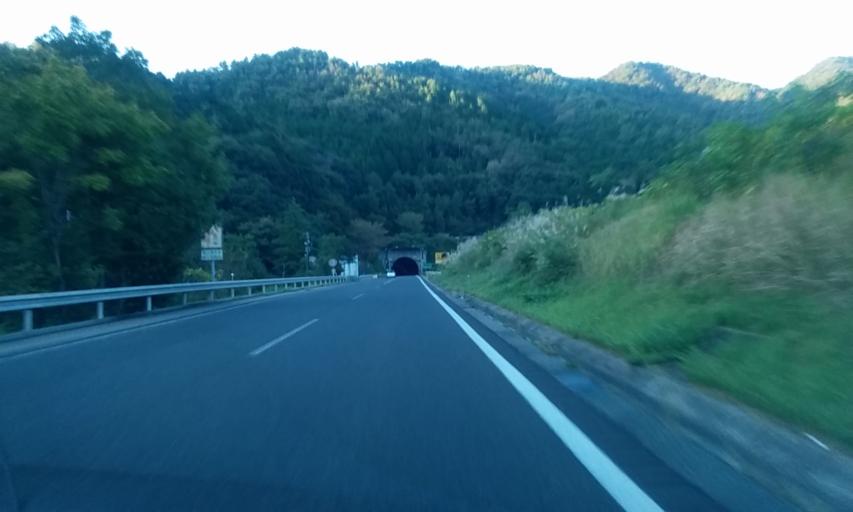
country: JP
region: Hyogo
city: Sasayama
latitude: 35.1138
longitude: 135.1654
